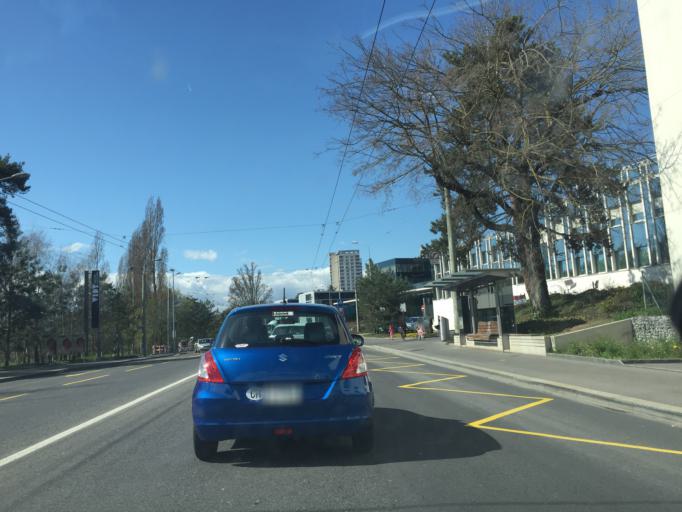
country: CH
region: Vaud
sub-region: Lausanne District
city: Lausanne
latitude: 46.5138
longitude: 6.6121
